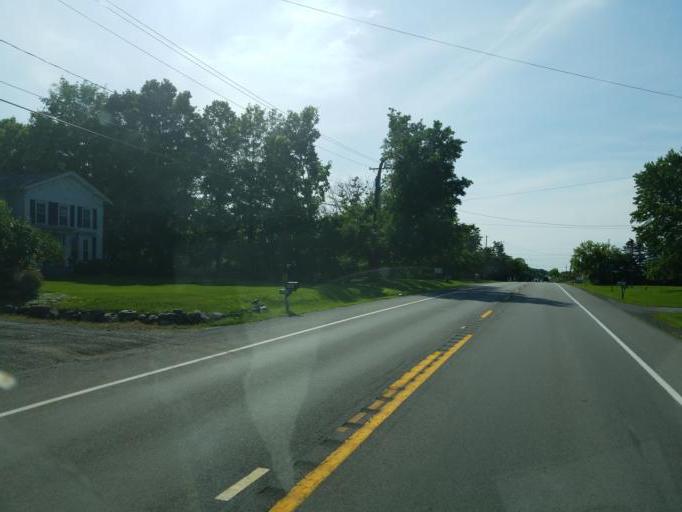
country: US
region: New York
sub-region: Livingston County
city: Avon
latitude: 42.9269
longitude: -77.7794
